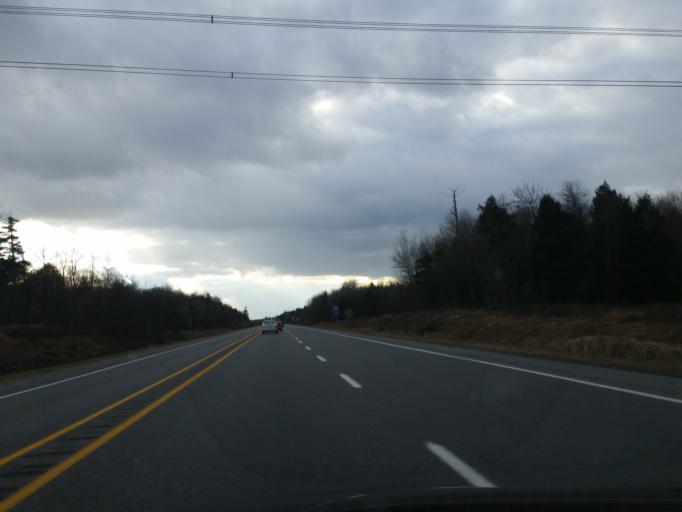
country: CA
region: Quebec
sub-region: Laurentides
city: Saint-Colomban
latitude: 45.6711
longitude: -74.1916
